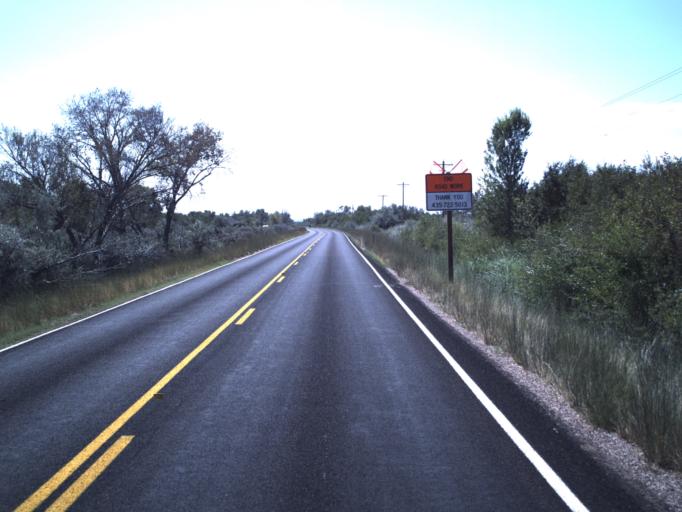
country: US
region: Utah
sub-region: Duchesne County
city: Roosevelt
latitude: 40.4315
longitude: -109.9281
